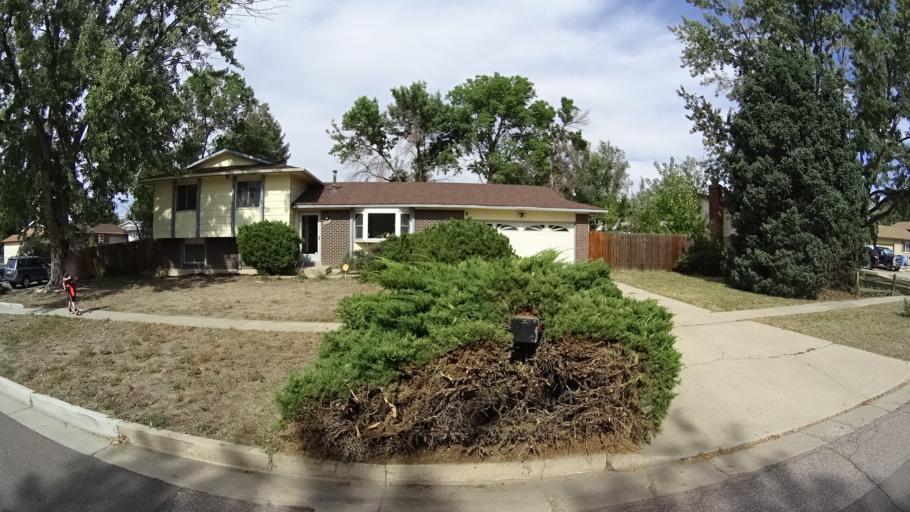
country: US
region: Colorado
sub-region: El Paso County
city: Cimarron Hills
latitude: 38.8968
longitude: -104.7679
